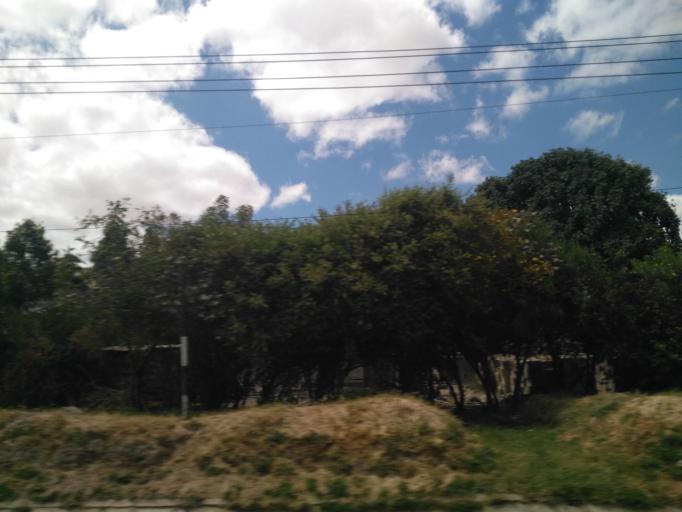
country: TZ
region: Dodoma
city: Dodoma
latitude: -6.1839
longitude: 35.7434
